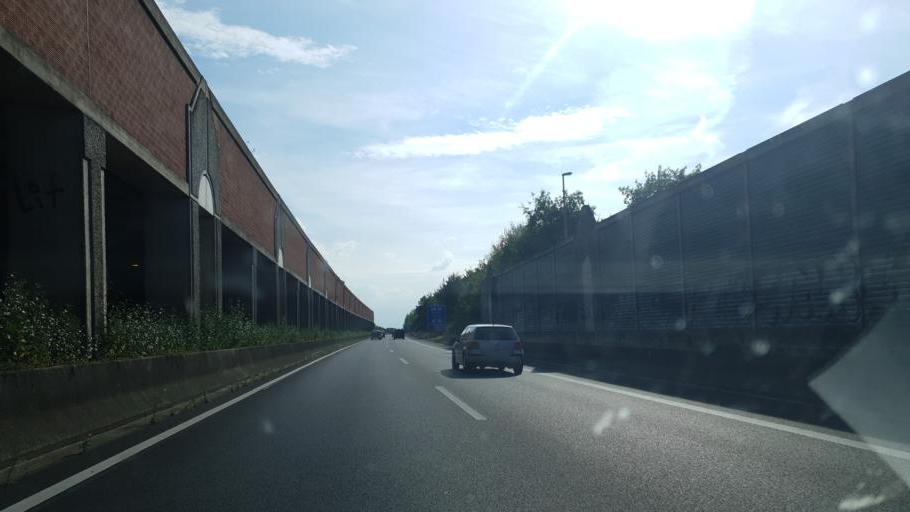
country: DE
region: Lower Saxony
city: Braunschweig
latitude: 52.2460
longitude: 10.5595
